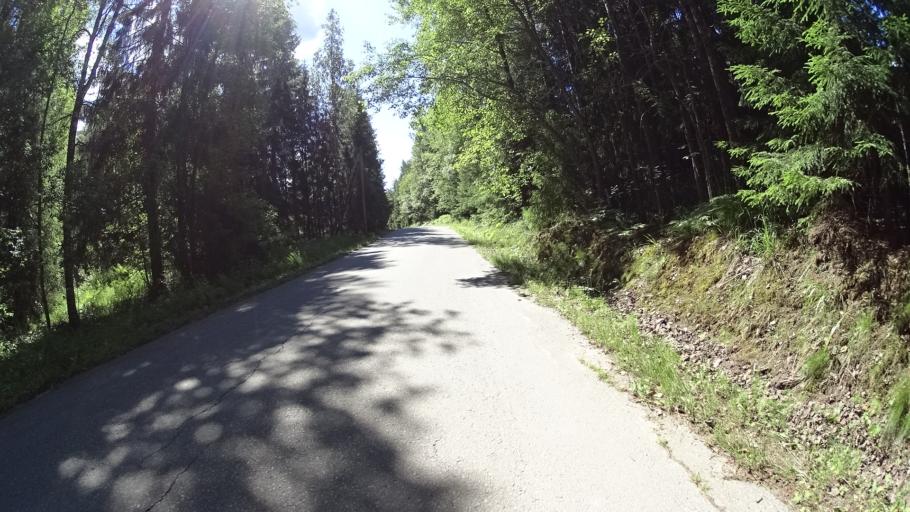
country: FI
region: Uusimaa
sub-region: Helsinki
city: Vihti
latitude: 60.3051
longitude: 24.4412
